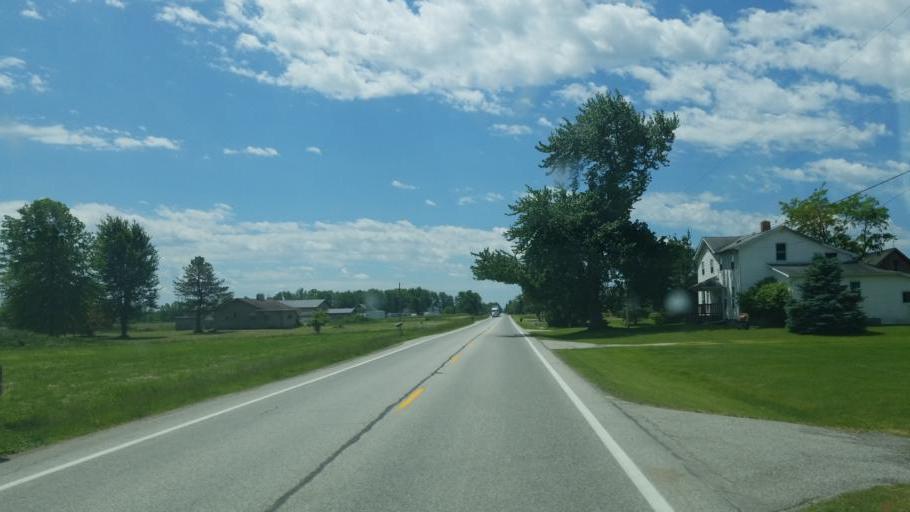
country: US
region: Ohio
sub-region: Geauga County
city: Middlefield
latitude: 41.4102
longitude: -80.9549
